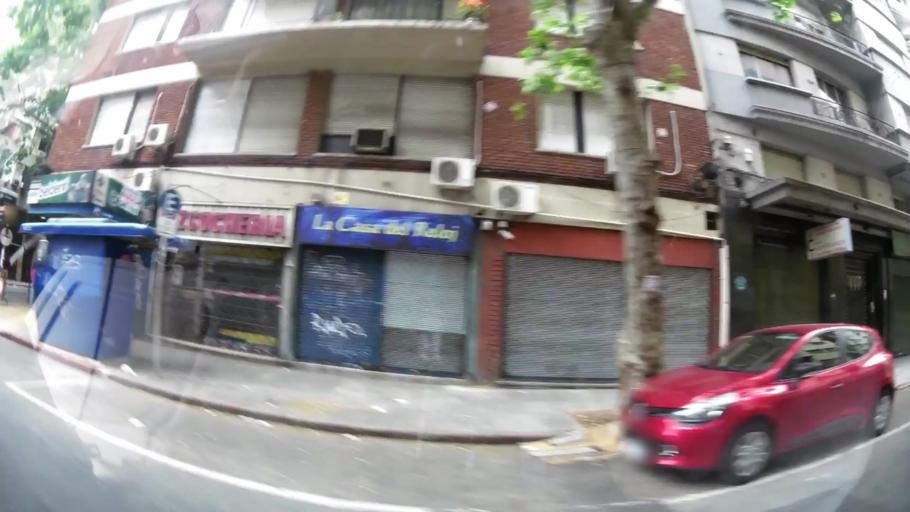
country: UY
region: Montevideo
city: Montevideo
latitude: -34.9045
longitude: -56.1983
